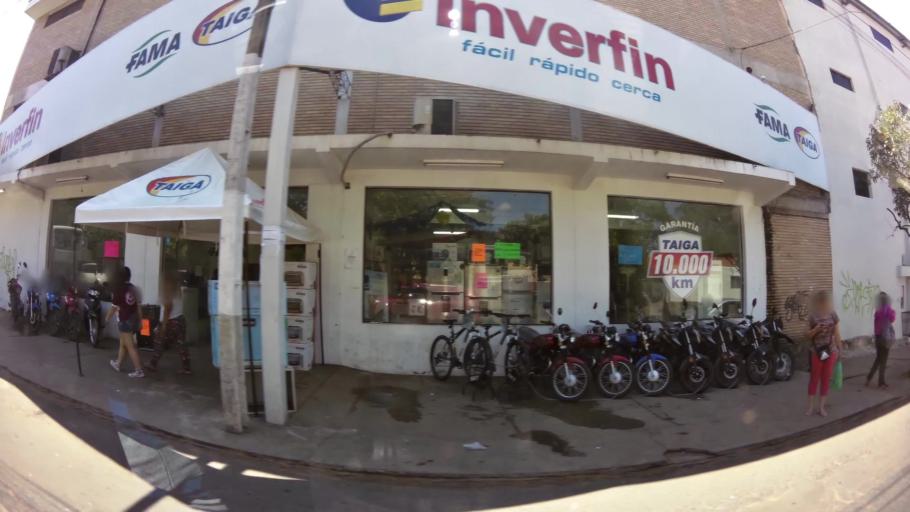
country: PY
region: Central
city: Nemby
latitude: -25.3946
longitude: -57.5470
